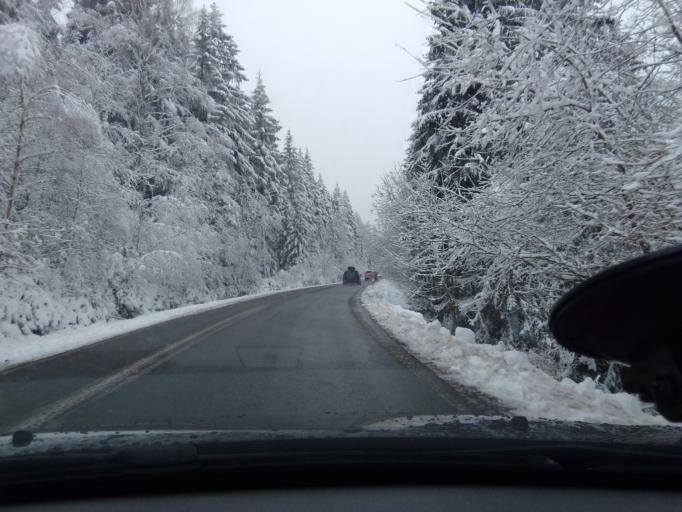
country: DE
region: Saxony
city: Markersbach
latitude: 50.5184
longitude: 12.8605
